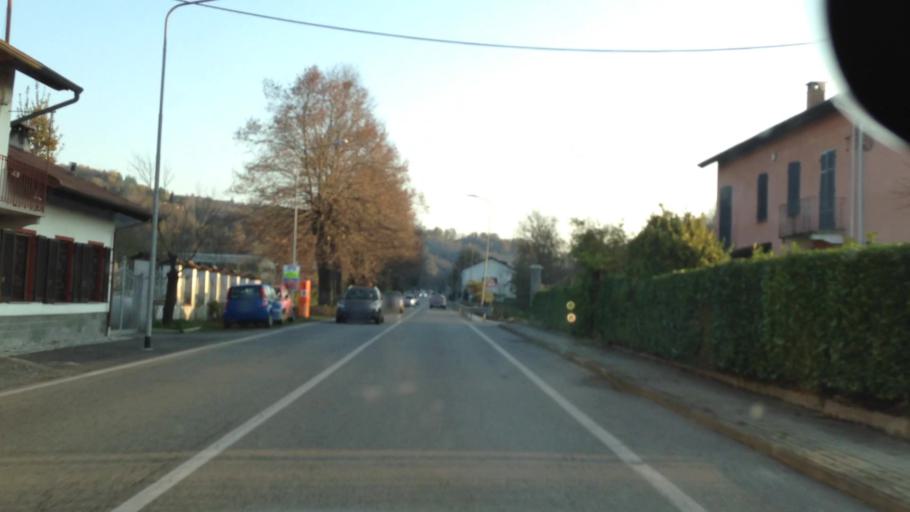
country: IT
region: Piedmont
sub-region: Provincia di Torino
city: Cavagnolo
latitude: 45.1499
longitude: 8.0530
